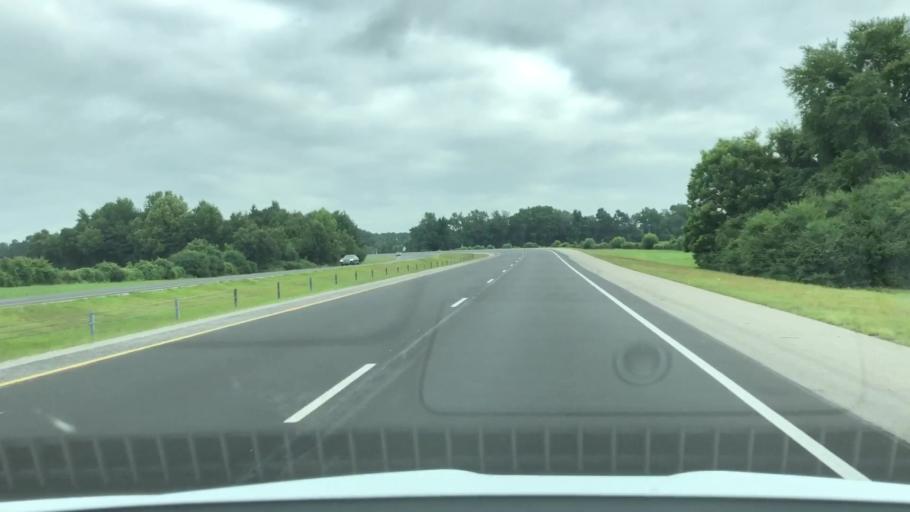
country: US
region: North Carolina
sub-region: Wayne County
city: Fremont
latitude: 35.5924
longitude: -77.9836
